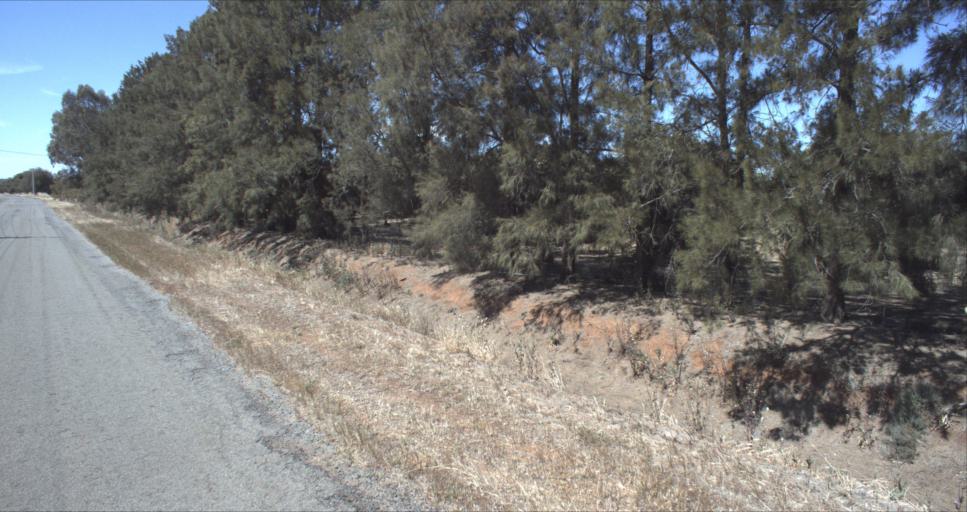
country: AU
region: New South Wales
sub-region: Leeton
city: Leeton
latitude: -34.6006
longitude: 146.4353
